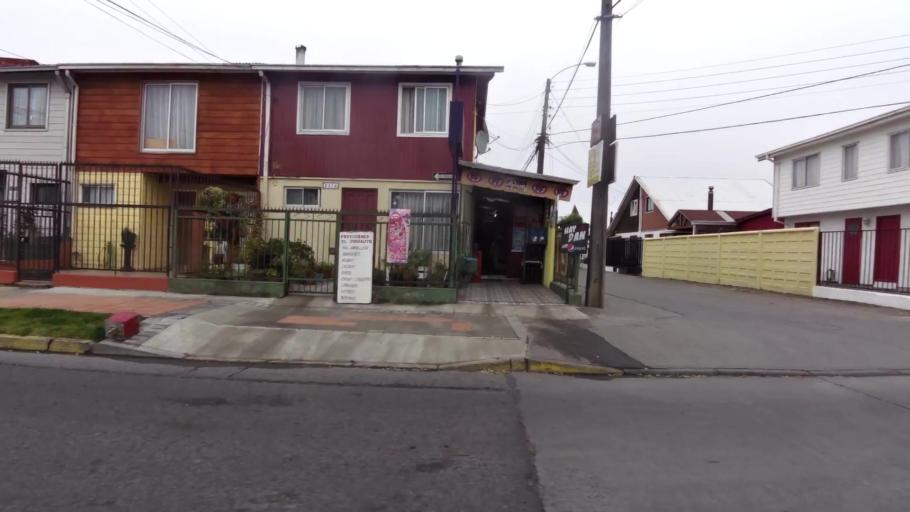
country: CL
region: Biobio
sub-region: Provincia de Concepcion
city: Concepcion
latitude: -36.7935
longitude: -73.0808
